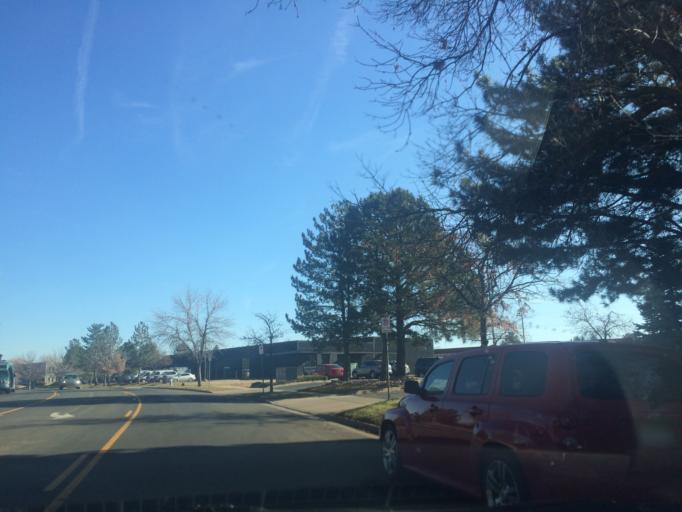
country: US
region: Colorado
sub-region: Boulder County
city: Boulder
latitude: 40.0225
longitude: -105.2203
